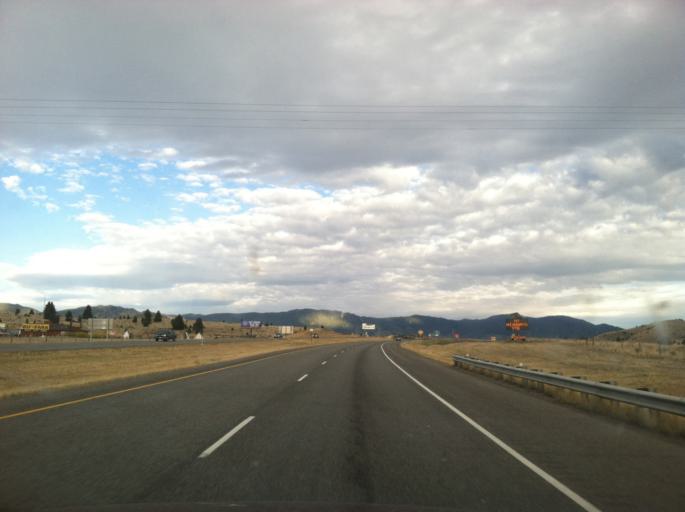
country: US
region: Montana
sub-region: Silver Bow County
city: Butte
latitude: 46.0087
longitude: -112.6271
